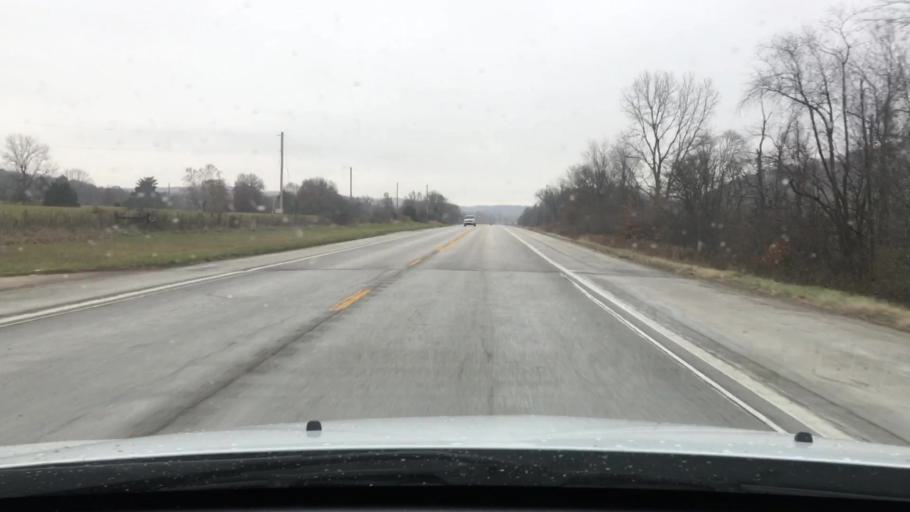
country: US
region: Missouri
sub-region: Pike County
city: Louisiana
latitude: 39.3988
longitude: -91.1107
